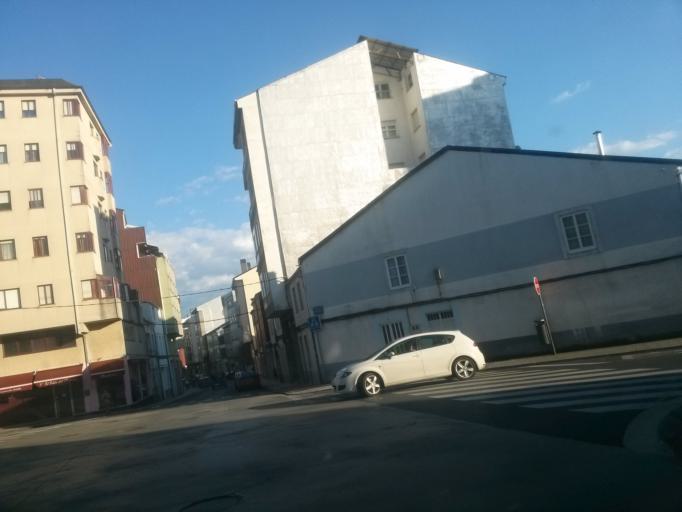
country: ES
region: Galicia
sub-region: Provincia de Lugo
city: Lugo
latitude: 43.0206
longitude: -7.5682
